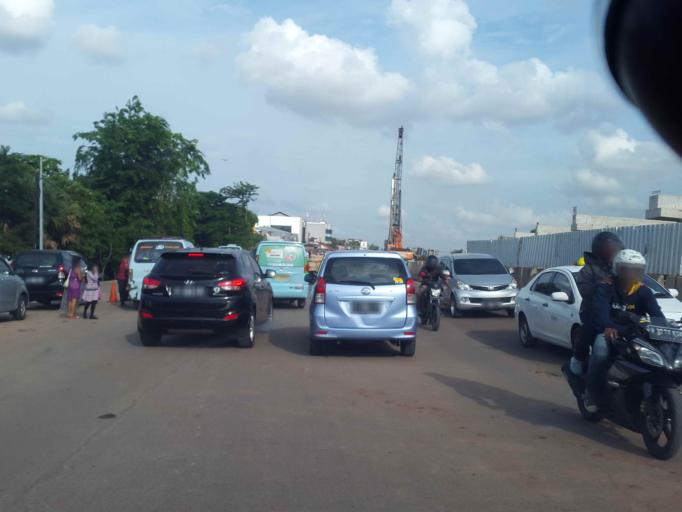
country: ID
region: West Java
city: Bekasi
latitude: -6.2476
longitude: 106.9207
